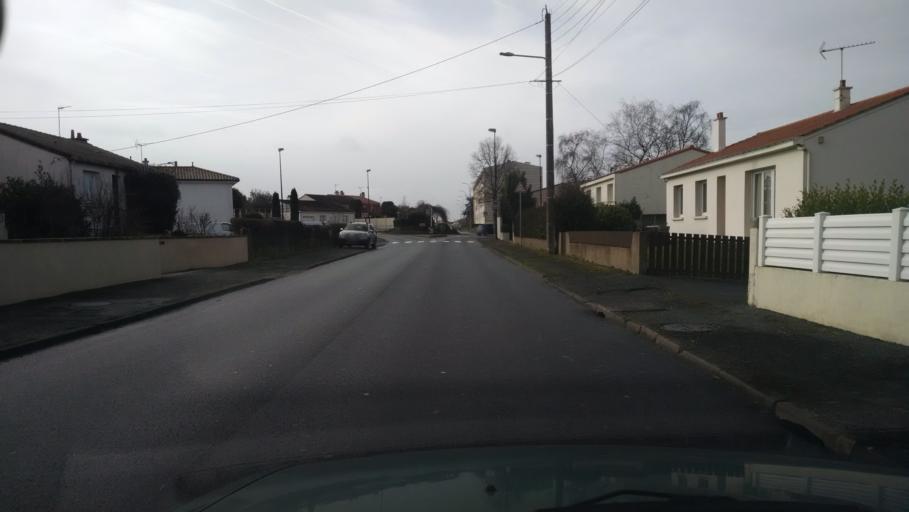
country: FR
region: Pays de la Loire
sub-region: Departement de la Vendee
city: Montaigu
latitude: 46.9828
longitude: -1.3050
